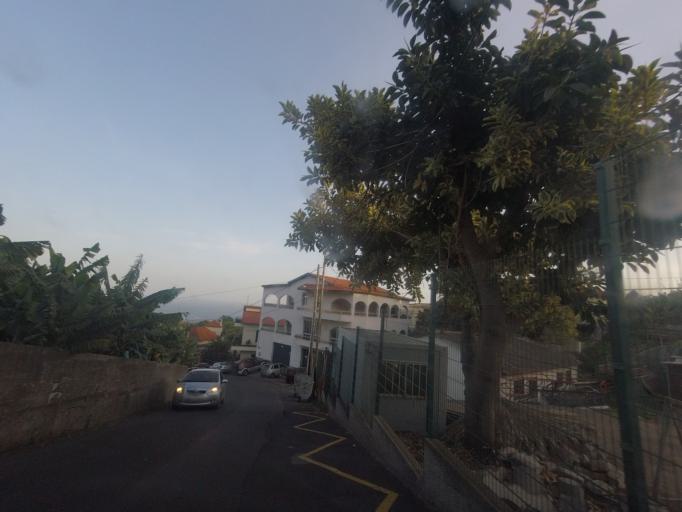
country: PT
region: Madeira
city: Camara de Lobos
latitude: 32.6526
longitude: -16.9860
